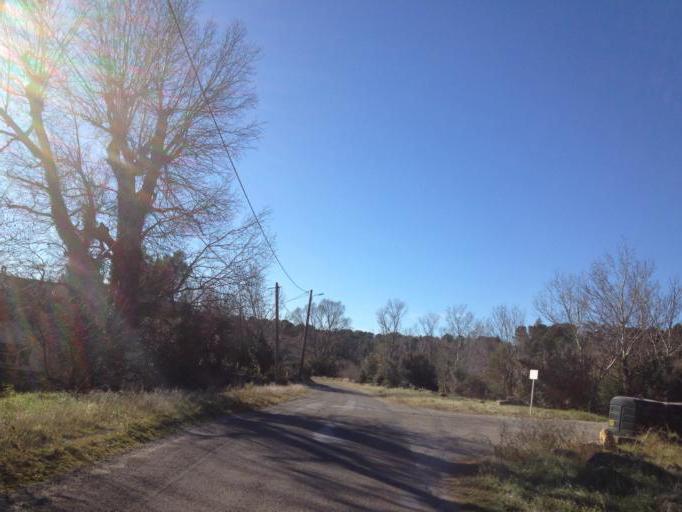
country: FR
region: Provence-Alpes-Cote d'Azur
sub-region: Departement du Vaucluse
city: Orange
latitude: 44.1266
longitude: 4.8100
